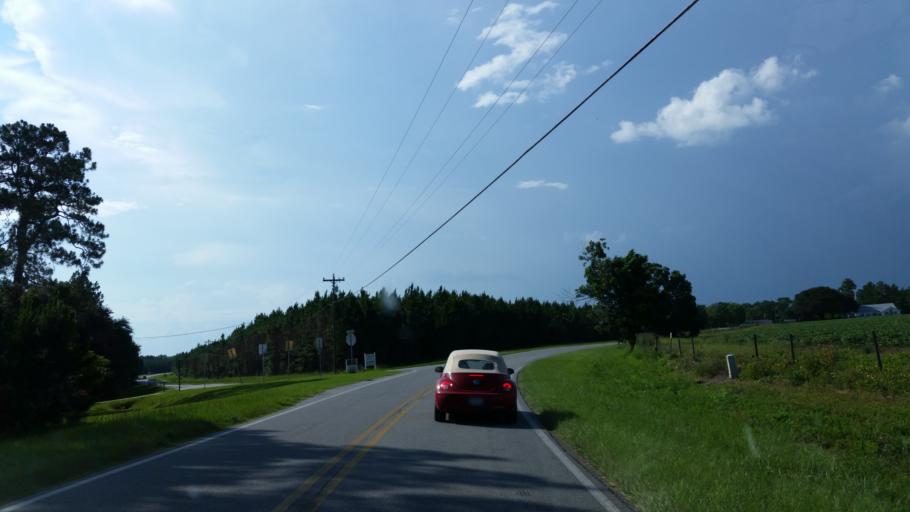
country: US
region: Georgia
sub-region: Lowndes County
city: Hahira
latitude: 30.9349
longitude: -83.4082
